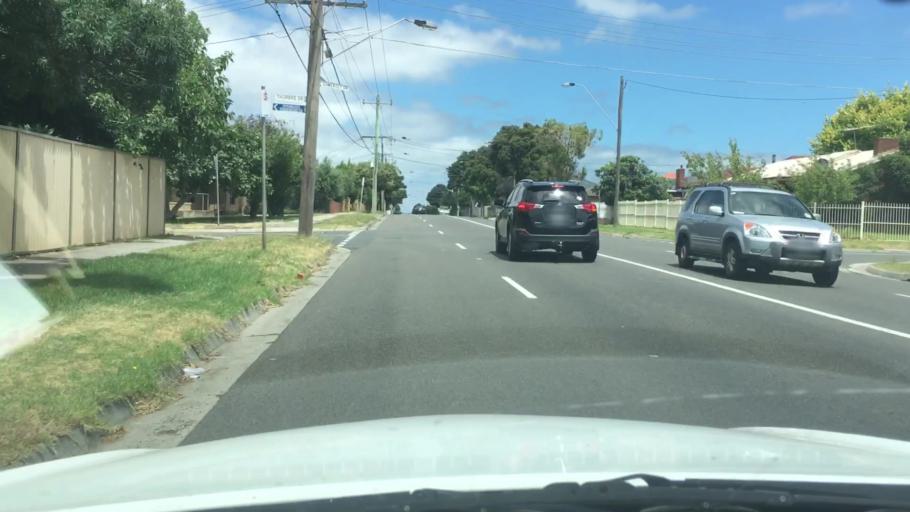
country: AU
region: Victoria
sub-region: Greater Dandenong
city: Keysborough
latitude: -37.9871
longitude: 145.1834
